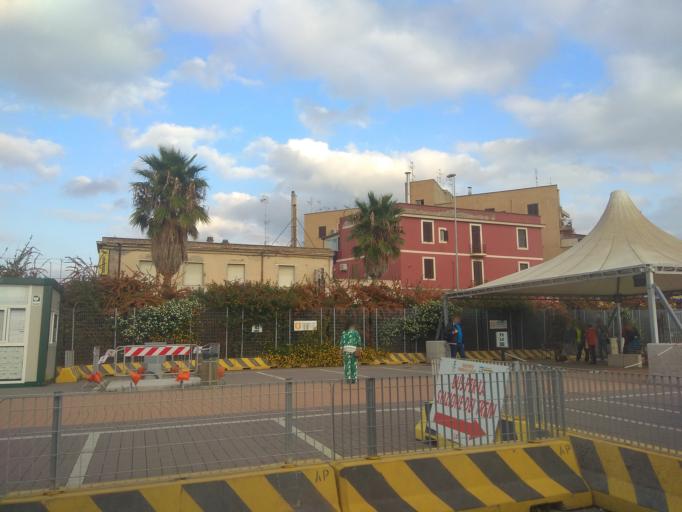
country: IT
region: Latium
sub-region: Citta metropolitana di Roma Capitale
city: Civitavecchia
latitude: 42.0975
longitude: 11.7887
